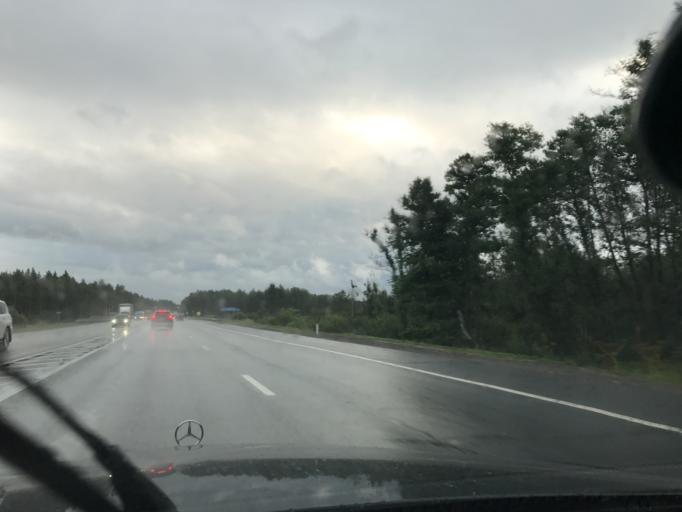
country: RU
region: Moskovskaya
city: Malaya Dubna
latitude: 55.8658
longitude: 38.9161
